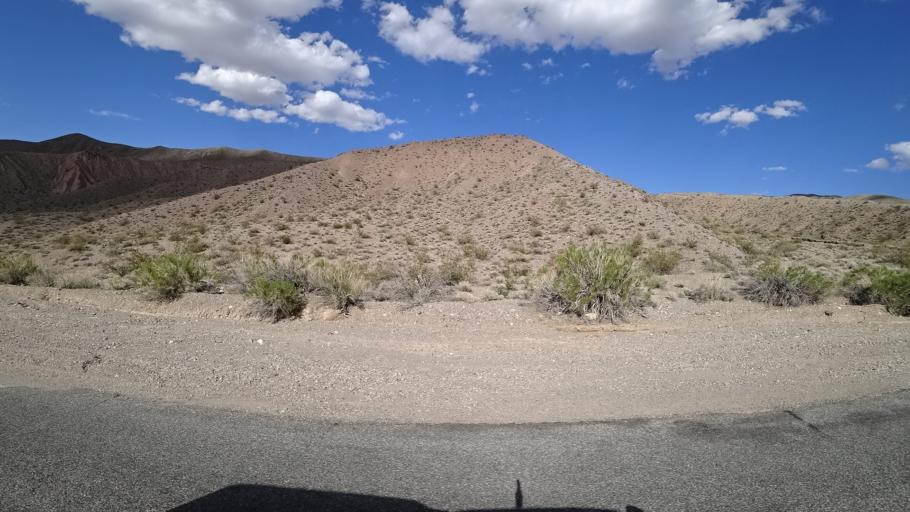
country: US
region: Nevada
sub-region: Nye County
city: Beatty
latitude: 36.4447
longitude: -117.1977
